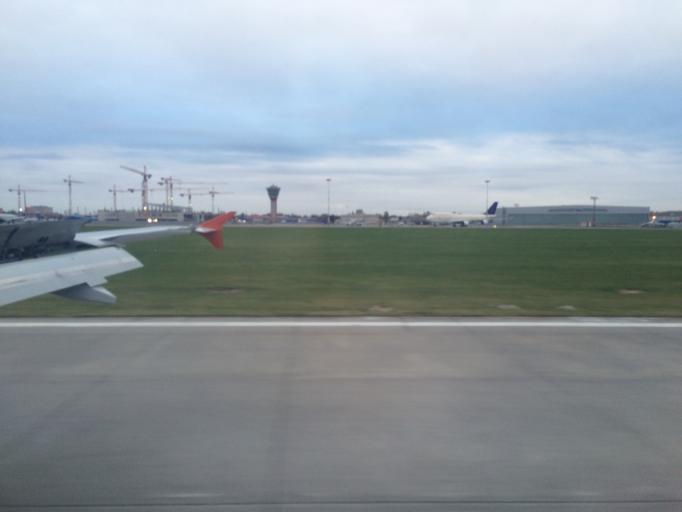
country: RU
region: Moskovskaya
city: Lobnya
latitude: 55.9750
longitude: 37.4223
